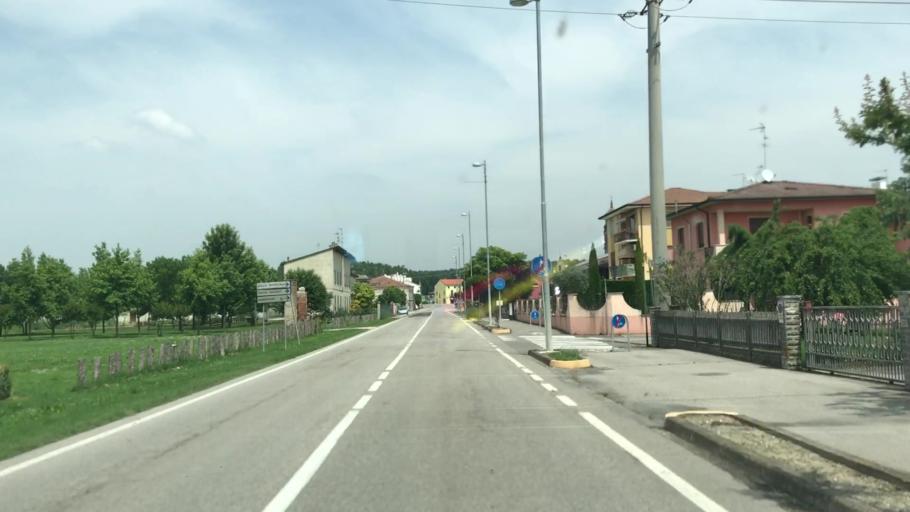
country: IT
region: Lombardy
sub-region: Provincia di Mantova
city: Carbonara di Po
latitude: 45.0349
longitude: 11.2257
